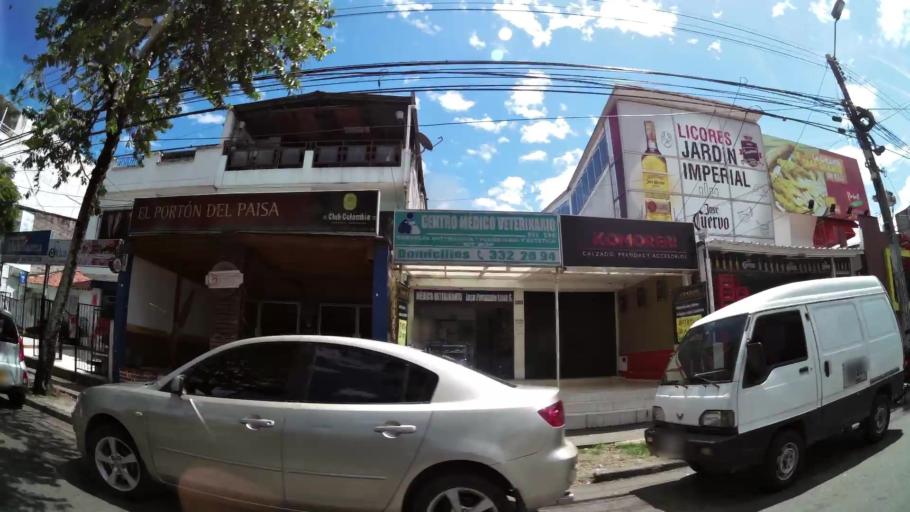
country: CO
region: Valle del Cauca
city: Cali
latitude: 3.3838
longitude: -76.5234
